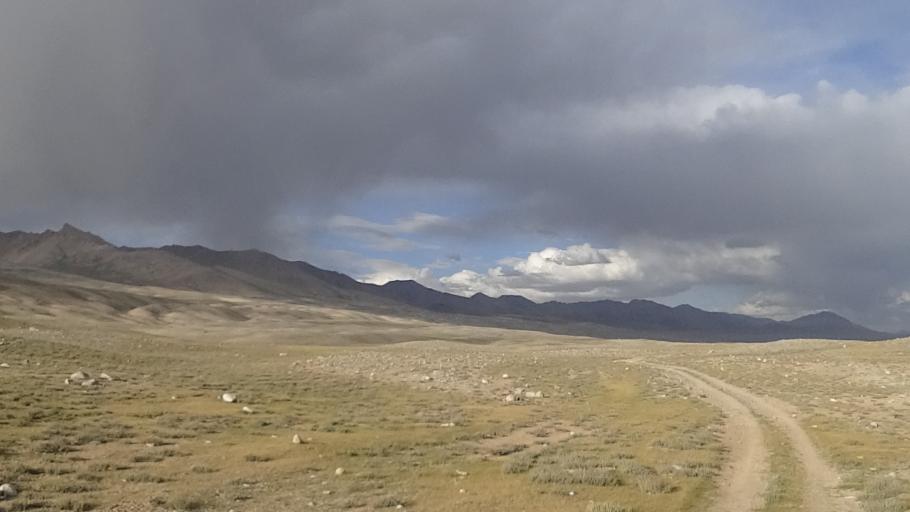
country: TJ
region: Gorno-Badakhshan
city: Murghob
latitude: 37.4623
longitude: 73.6204
